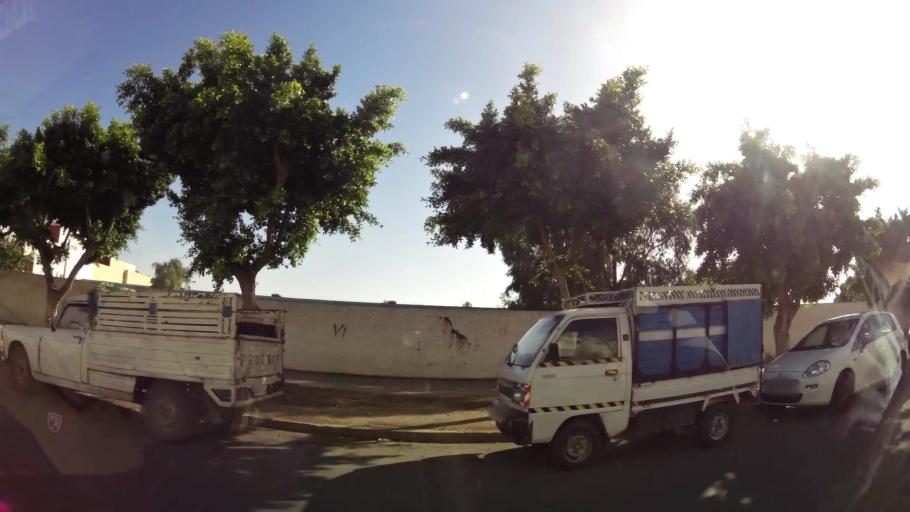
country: MA
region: Souss-Massa-Draa
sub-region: Agadir-Ida-ou-Tnan
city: Agadir
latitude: 30.4272
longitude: -9.5784
